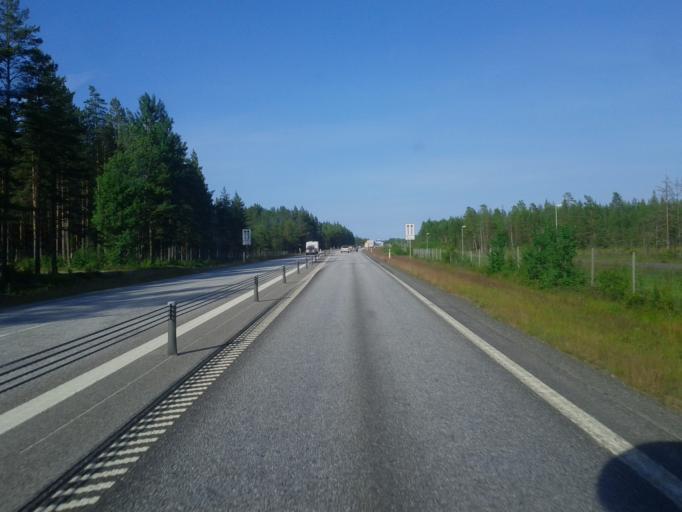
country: SE
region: Vaesterbotten
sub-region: Umea Kommun
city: Taftea
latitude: 63.8817
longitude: 20.4880
